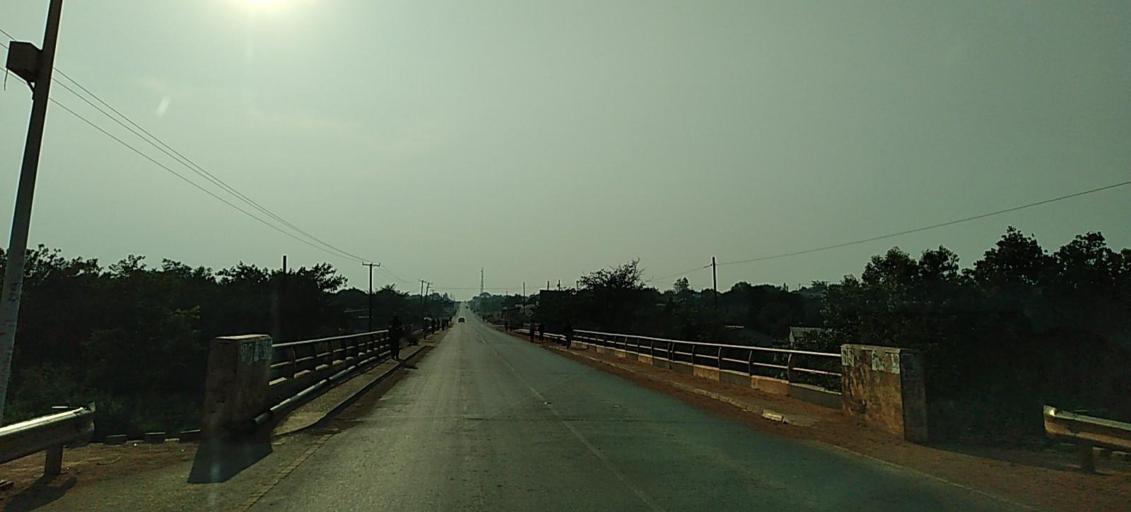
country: ZM
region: North-Western
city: Solwezi
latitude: -12.1887
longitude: 26.4316
